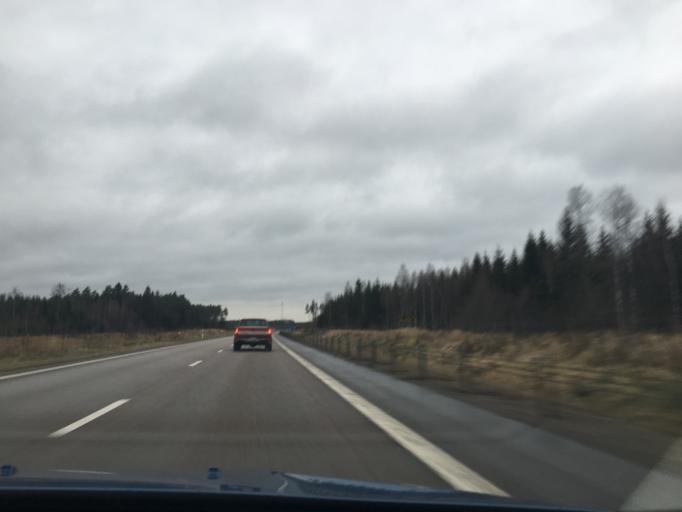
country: SE
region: Uppsala
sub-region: Tierps Kommun
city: Tierp
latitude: 60.4311
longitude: 17.4287
